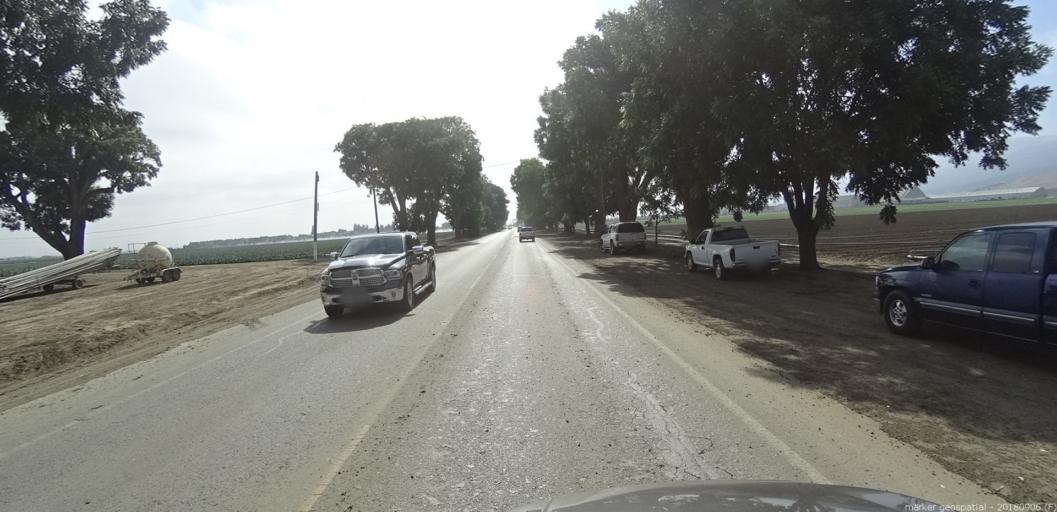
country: US
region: California
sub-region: Monterey County
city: Salinas
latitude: 36.6265
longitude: -121.6578
